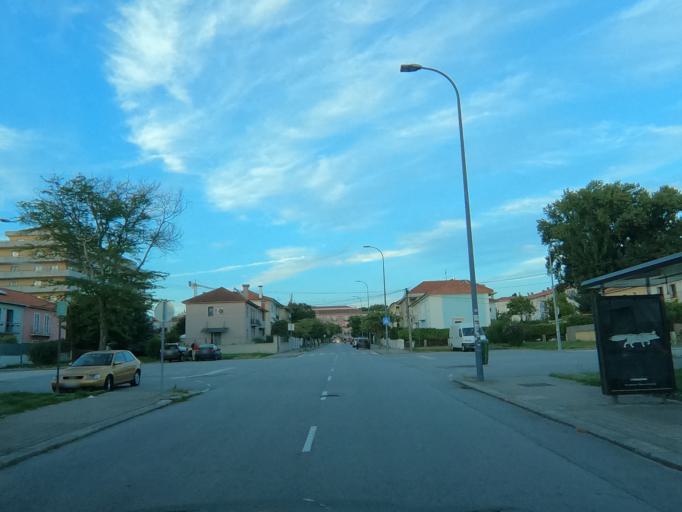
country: PT
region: Porto
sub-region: Porto
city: Porto
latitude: 41.1753
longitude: -8.6168
